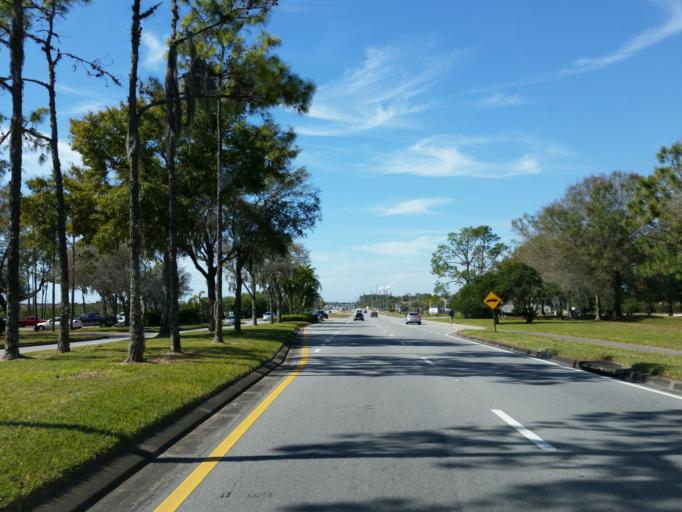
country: US
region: Florida
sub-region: Hillsborough County
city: Balm
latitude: 27.7922
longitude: -82.3272
